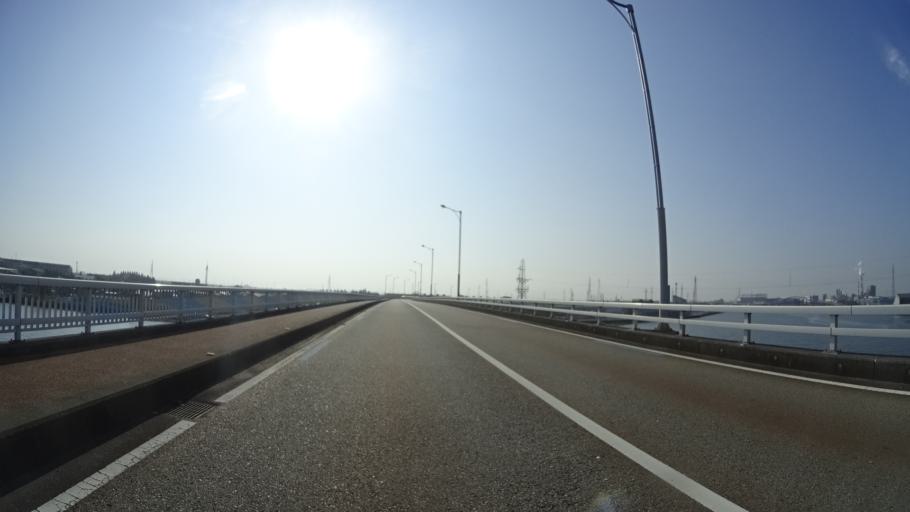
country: JP
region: Toyama
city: Nishishinminato
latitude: 36.7890
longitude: 137.0583
